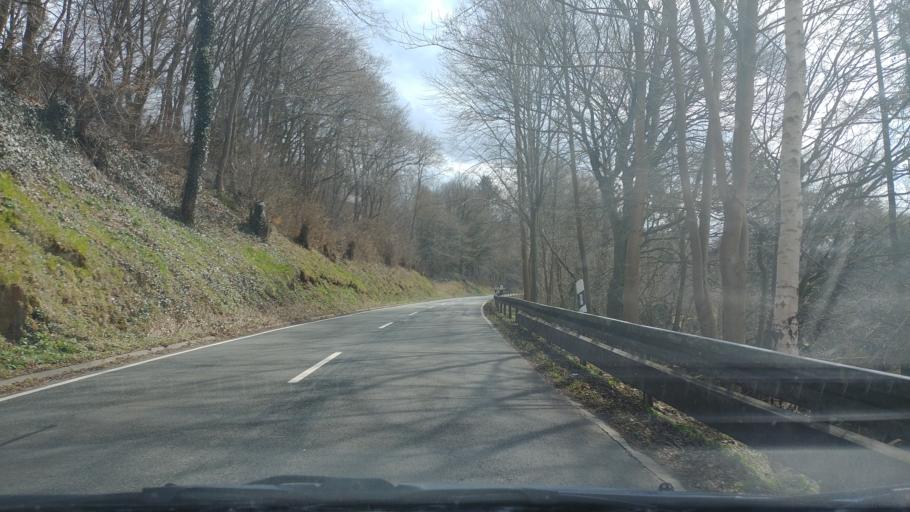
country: DE
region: Lower Saxony
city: Furstenberg
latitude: 51.7472
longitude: 9.4038
